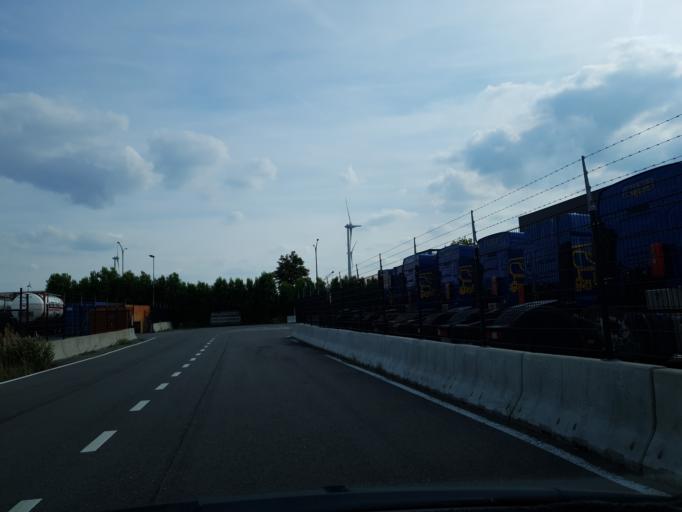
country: BE
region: Flanders
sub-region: Provincie Antwerpen
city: Antwerpen
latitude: 51.2655
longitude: 4.3951
